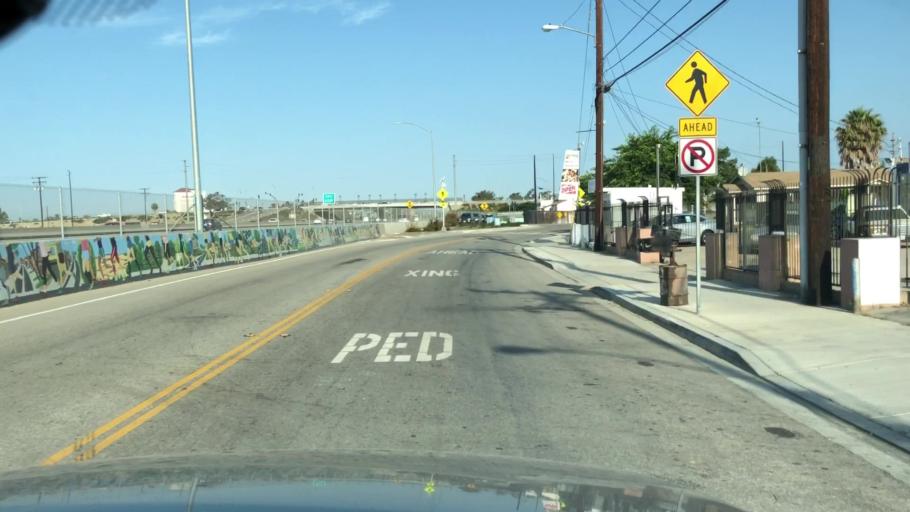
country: US
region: California
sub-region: Ventura County
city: El Rio
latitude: 34.2226
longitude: -119.1378
